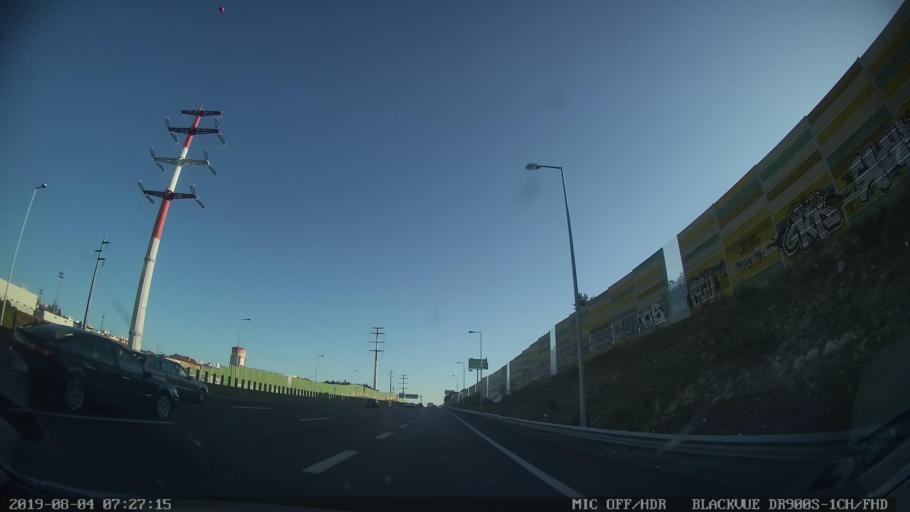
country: PT
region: Lisbon
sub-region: Loures
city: Santa Iria da Azoia
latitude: 38.8466
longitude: -9.0923
